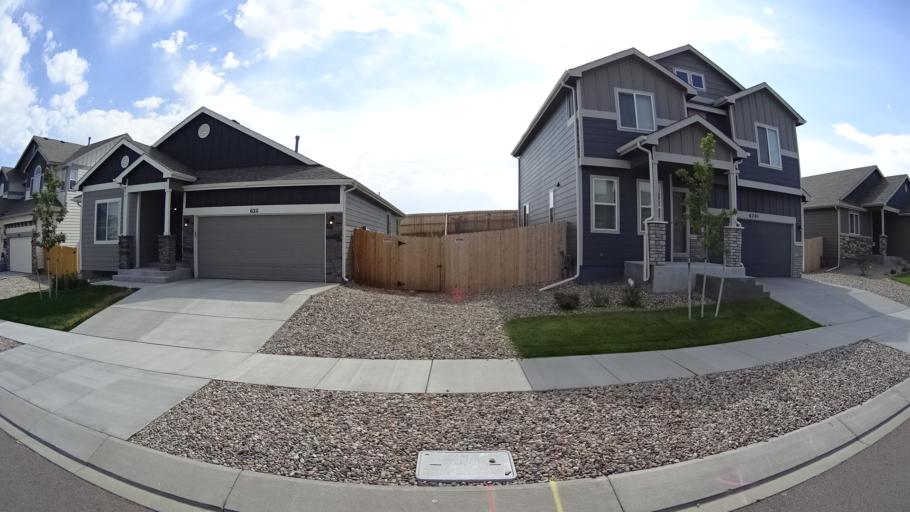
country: US
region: Colorado
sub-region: El Paso County
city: Cimarron Hills
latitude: 38.9211
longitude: -104.6810
